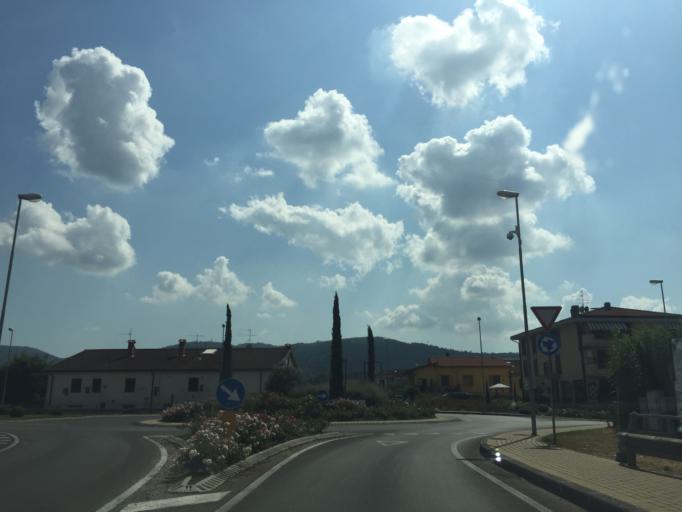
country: IT
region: Tuscany
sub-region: Provincia di Pistoia
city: Cantagrillo-Casalguidi
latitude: 43.8833
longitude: 10.9168
